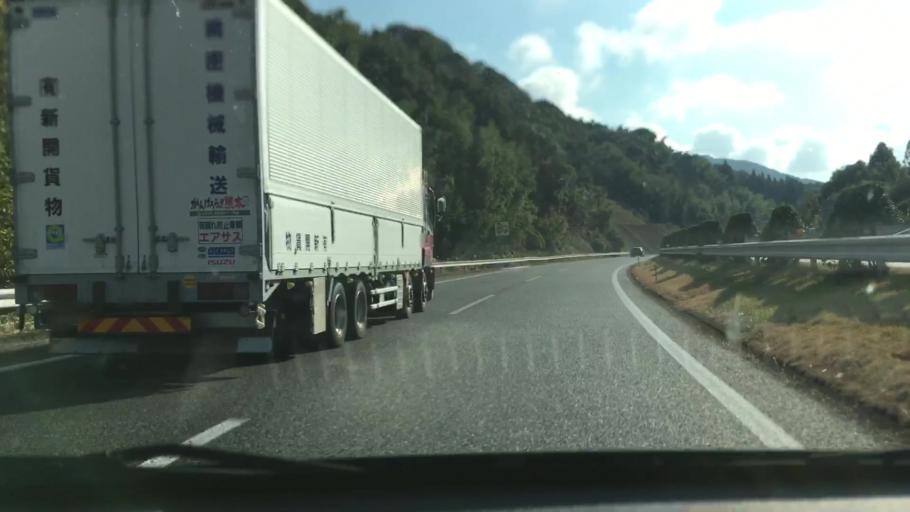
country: JP
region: Kumamoto
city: Matsubase
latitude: 32.6114
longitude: 130.7247
